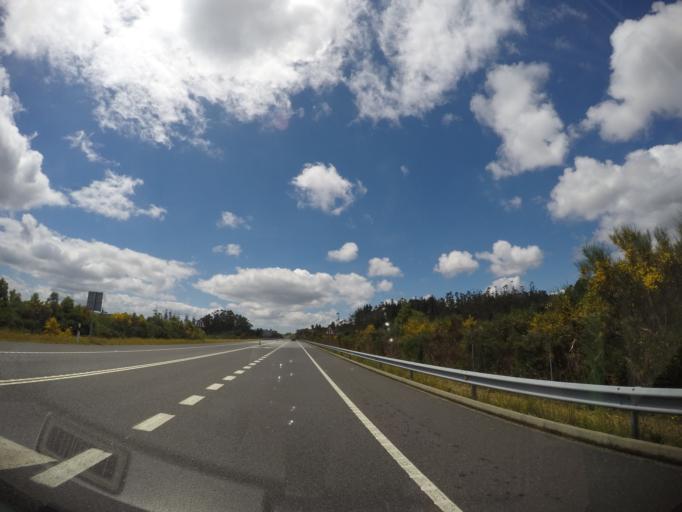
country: ES
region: Aragon
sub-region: Provincia de Zaragoza
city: Monegrillo
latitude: 41.5358
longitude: -0.4051
